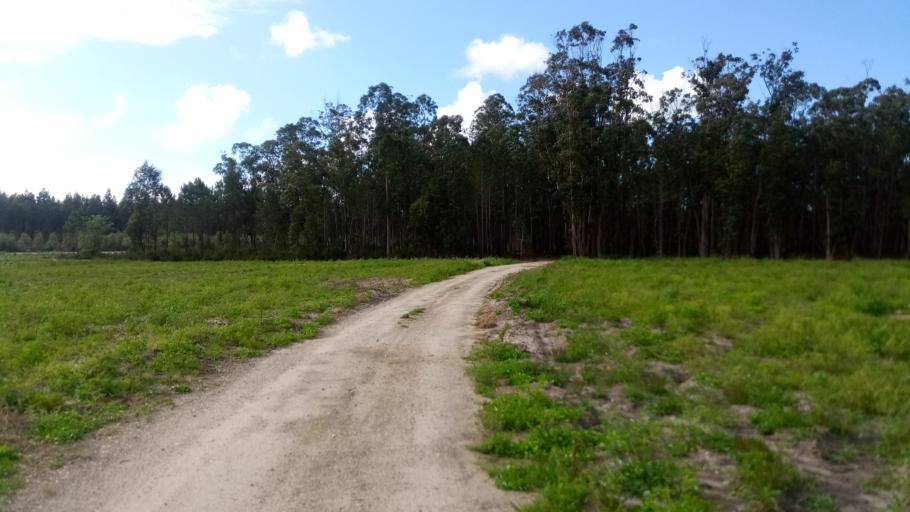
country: PT
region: Leiria
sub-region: Caldas da Rainha
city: Caldas da Rainha
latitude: 39.4353
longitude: -9.1658
